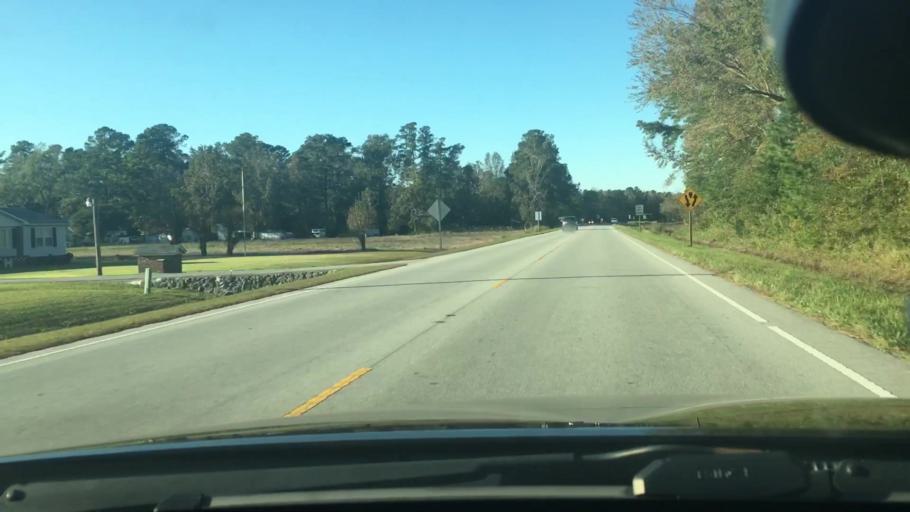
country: US
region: North Carolina
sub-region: Craven County
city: Vanceboro
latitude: 35.3292
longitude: -77.1491
